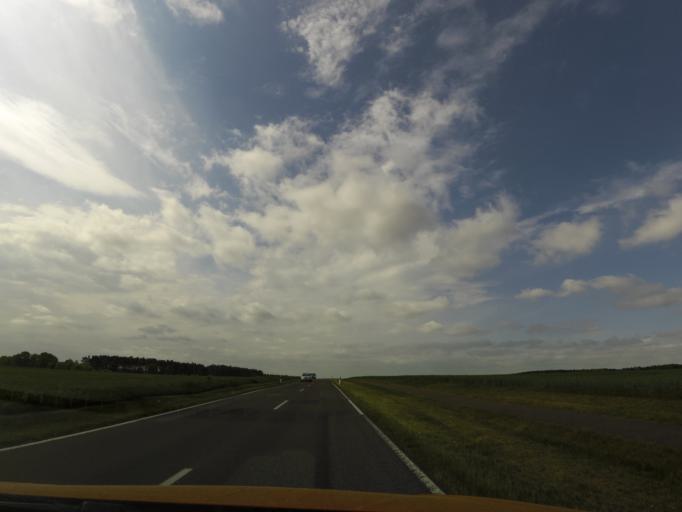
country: DE
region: Brandenburg
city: Belzig
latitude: 52.0878
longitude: 12.5375
